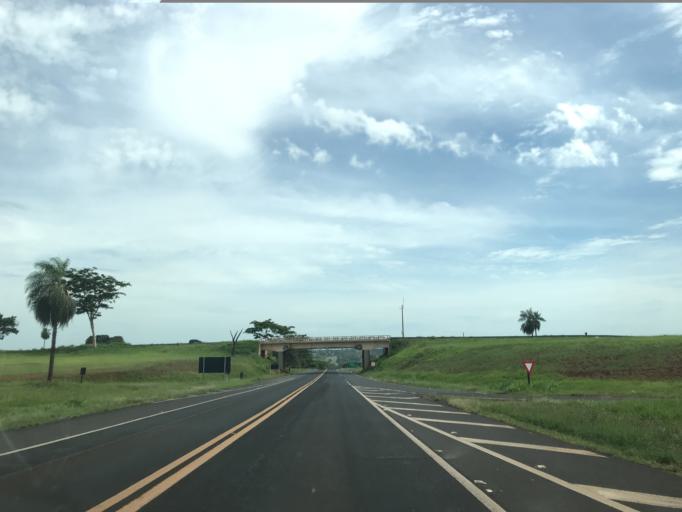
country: BR
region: Sao Paulo
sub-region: Nova Granada
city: Nova Granada
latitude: -20.3264
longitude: -49.2120
